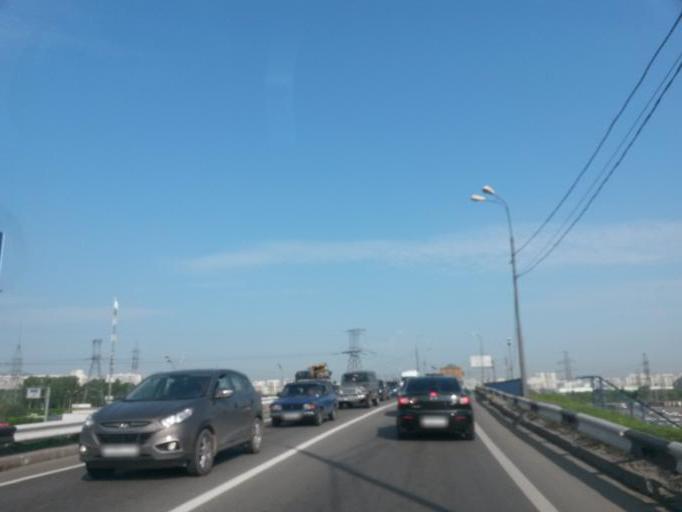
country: RU
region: Moscow
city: Zyablikovo
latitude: 55.6173
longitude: 37.7832
